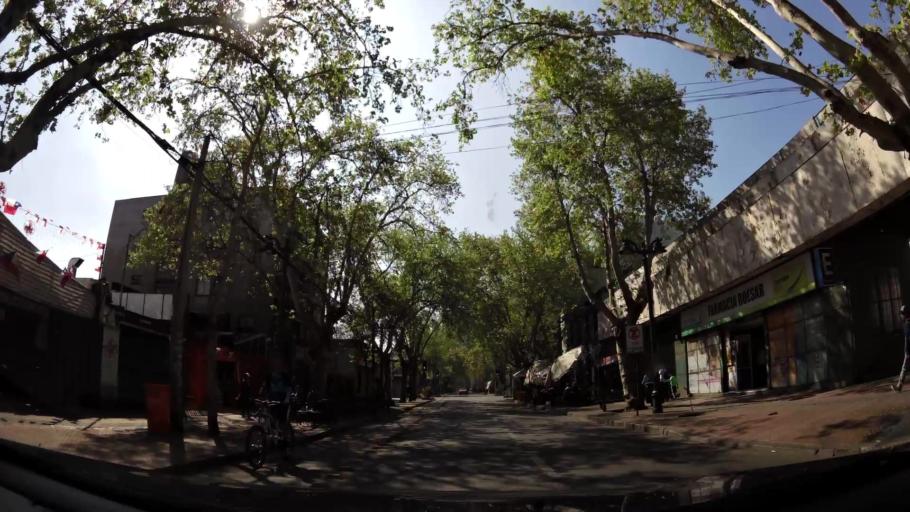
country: CL
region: Santiago Metropolitan
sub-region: Provincia de Santiago
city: Santiago
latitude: -33.4327
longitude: -70.6360
